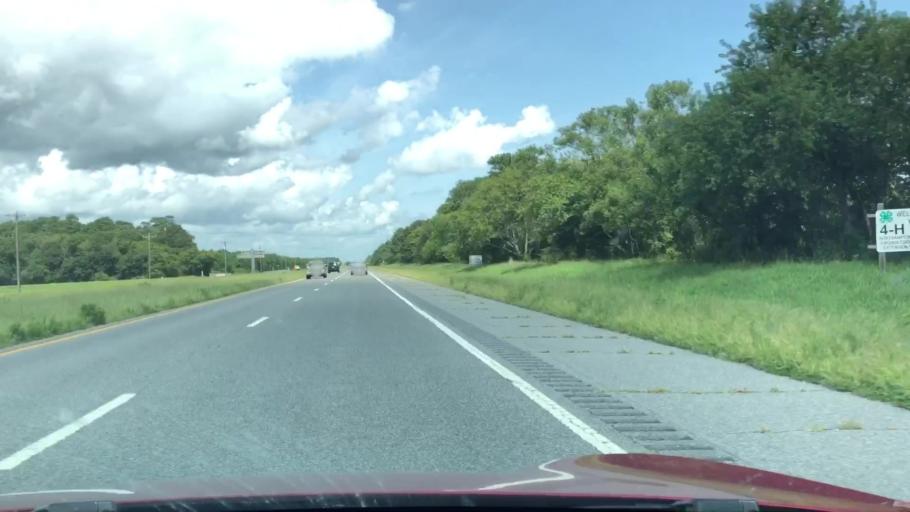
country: US
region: Virginia
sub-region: Northampton County
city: Cape Charles
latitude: 37.1521
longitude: -75.9715
